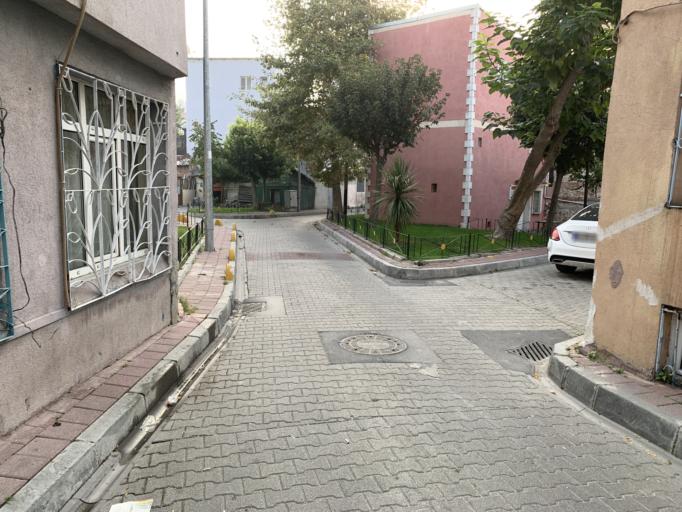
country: TR
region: Istanbul
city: Eminoenue
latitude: 41.0033
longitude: 28.9683
